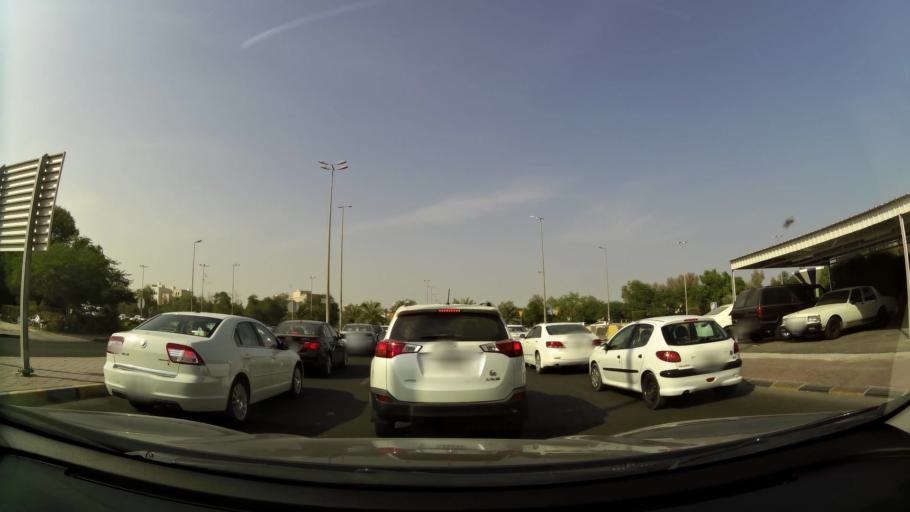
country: KW
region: Mubarak al Kabir
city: Mubarak al Kabir
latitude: 29.1742
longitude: 48.0846
